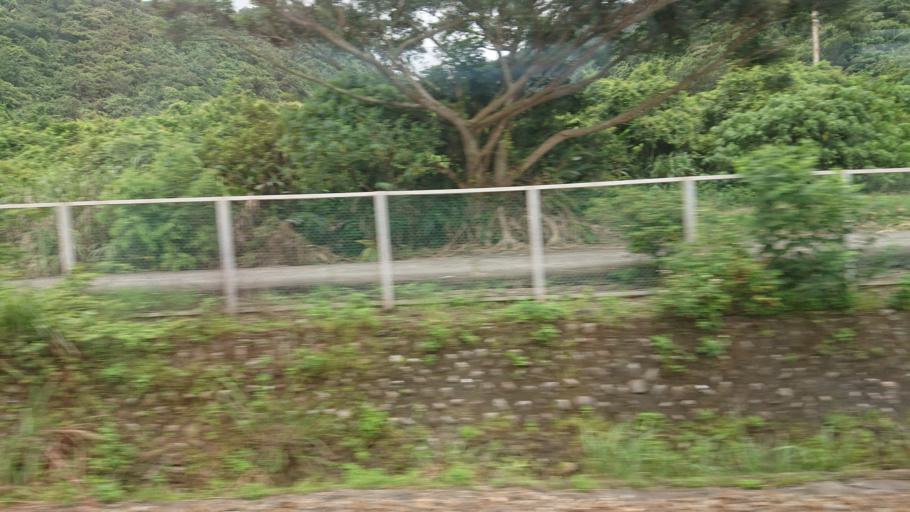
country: TW
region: Taiwan
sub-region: Keelung
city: Keelung
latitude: 24.9506
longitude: 121.9084
